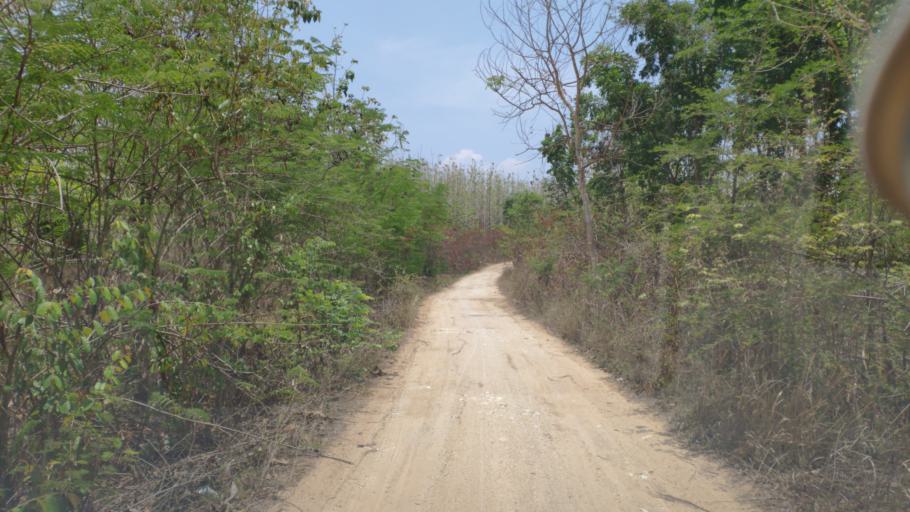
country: ID
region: Central Java
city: Botoh
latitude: -7.0551
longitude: 111.4871
